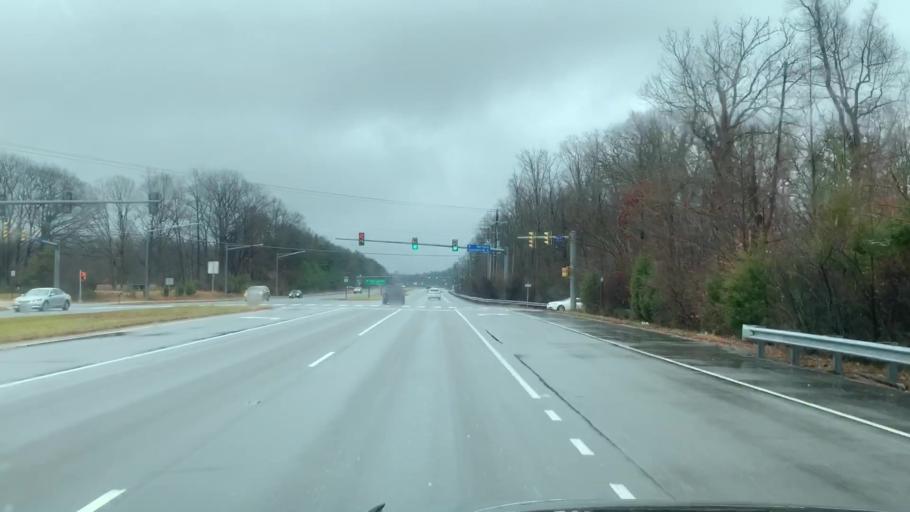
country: US
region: Virginia
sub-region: Fairfax County
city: Fairfax Station
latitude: 38.7629
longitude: -77.3107
